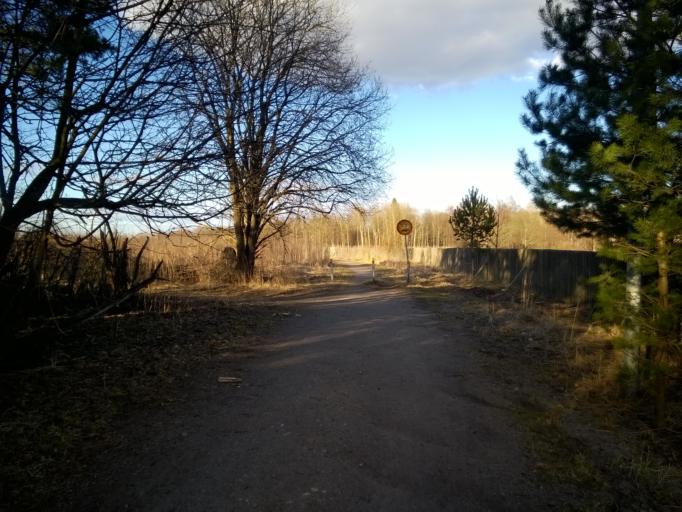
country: FI
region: Uusimaa
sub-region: Helsinki
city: Vantaa
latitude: 60.2452
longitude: 25.0405
